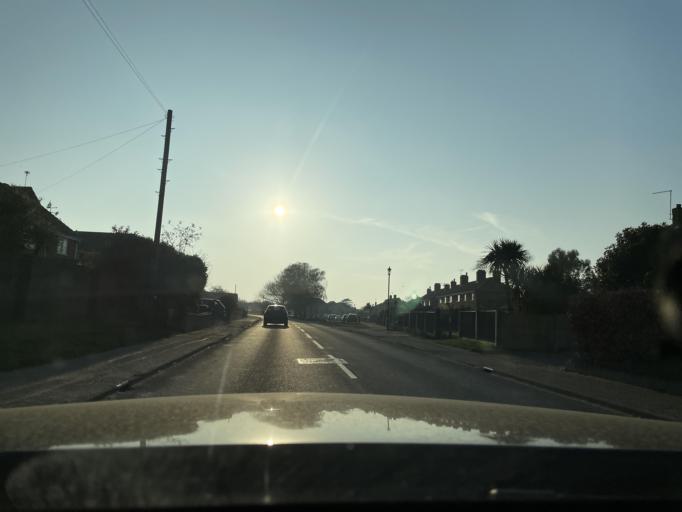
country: GB
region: England
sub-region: Norfolk
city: Martham
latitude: 52.7022
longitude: 1.6289
